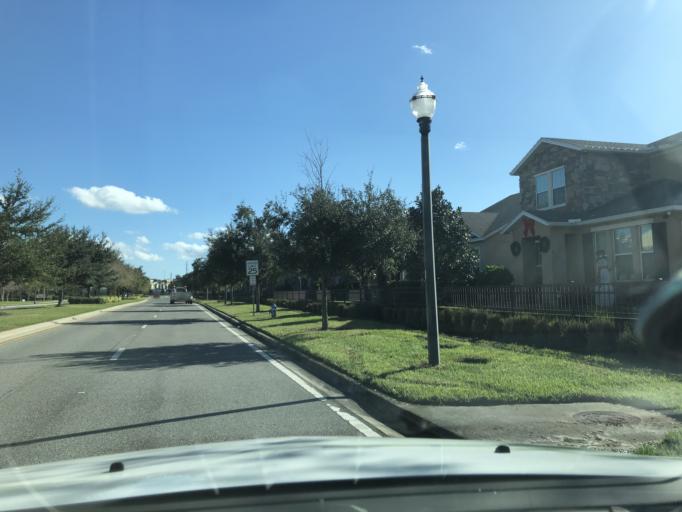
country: US
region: Florida
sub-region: Orange County
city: Oak Ridge
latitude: 28.4859
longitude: -81.4454
